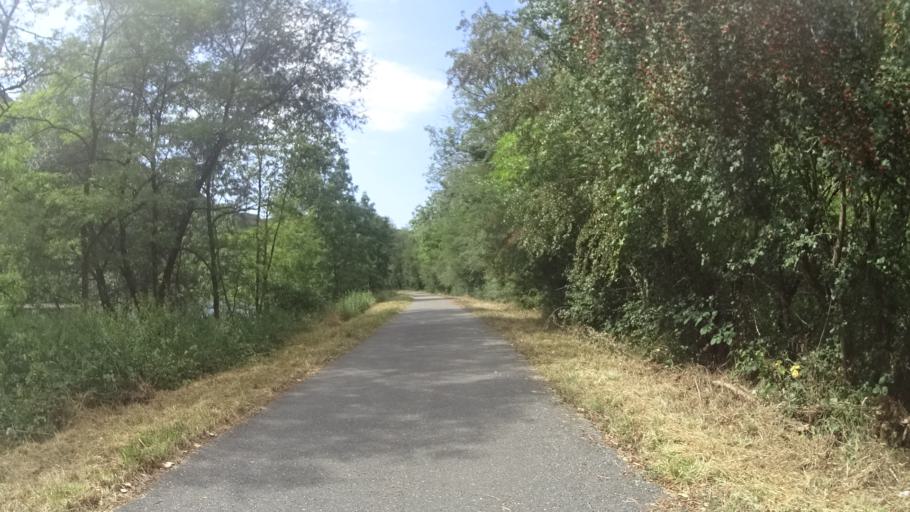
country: FR
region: Franche-Comte
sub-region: Departement du Doubs
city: Roulans
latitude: 47.2972
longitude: 6.2270
